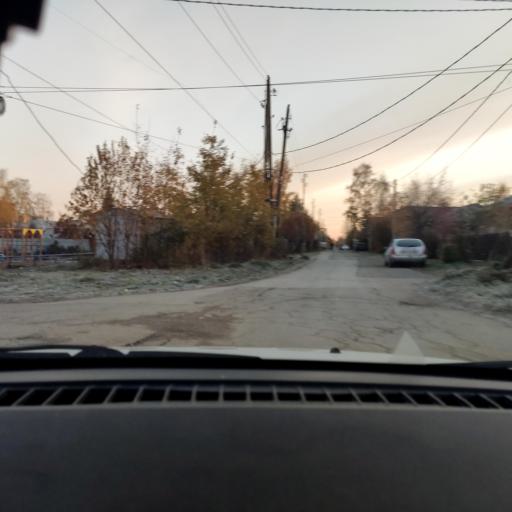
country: RU
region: Perm
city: Perm
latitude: 58.0551
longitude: 56.3600
